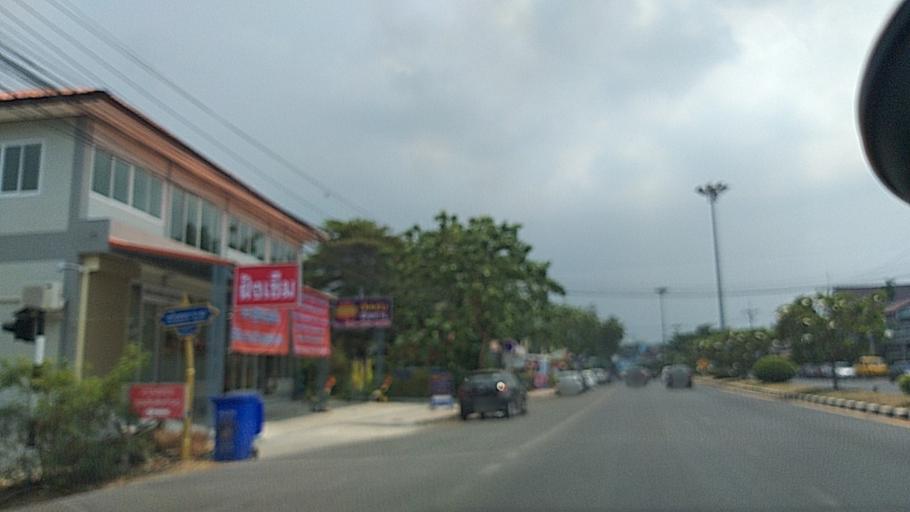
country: TH
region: Phra Nakhon Si Ayutthaya
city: Phra Nakhon Si Ayutthaya
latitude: 14.3483
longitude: 100.5919
